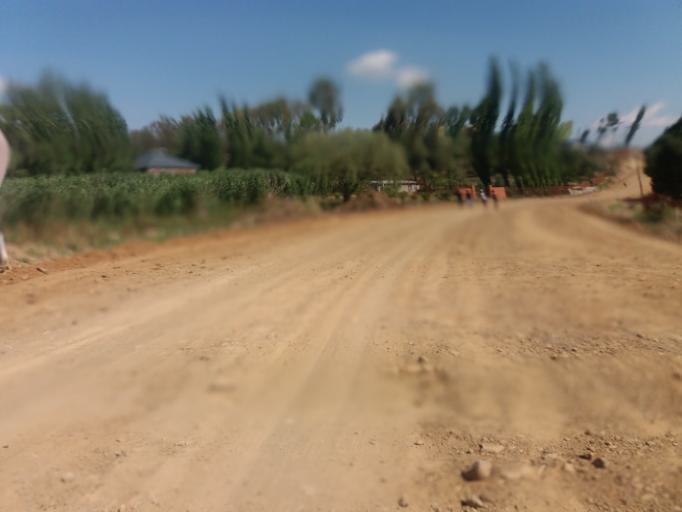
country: LS
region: Maseru
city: Maseru
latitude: -29.3197
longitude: 27.5043
